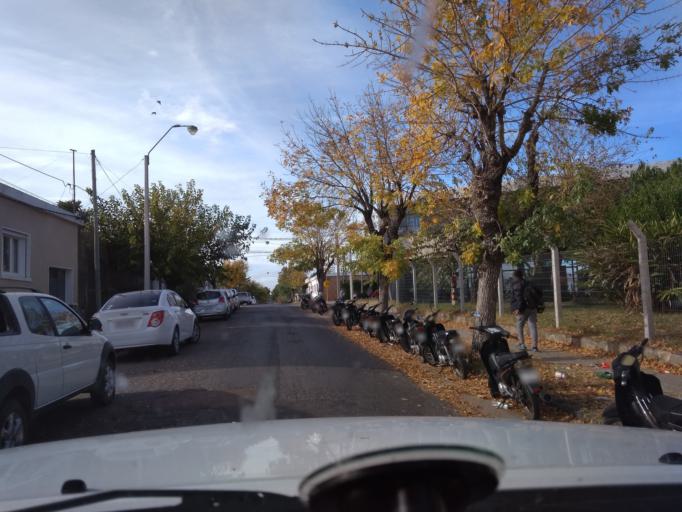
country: UY
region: Florida
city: Florida
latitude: -34.0987
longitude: -56.2216
